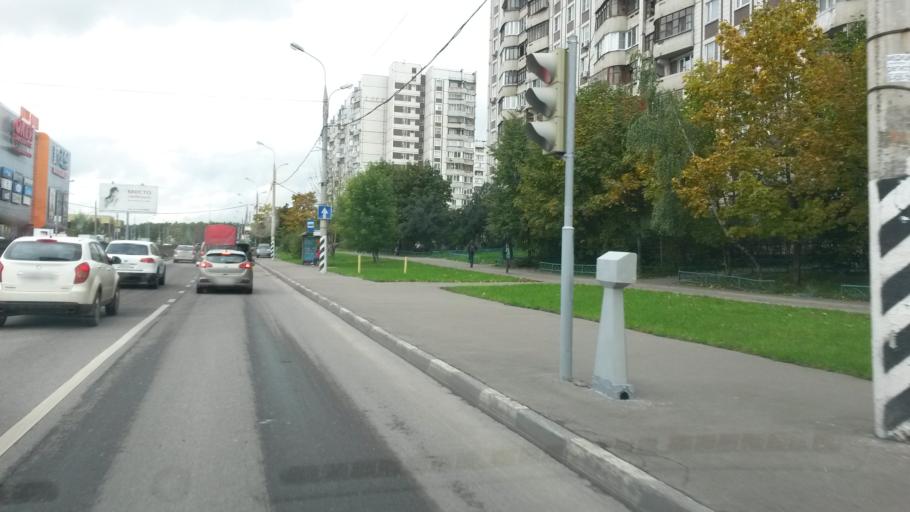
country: RU
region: Moskovskaya
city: Shcherbinka
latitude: 55.5469
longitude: 37.5456
